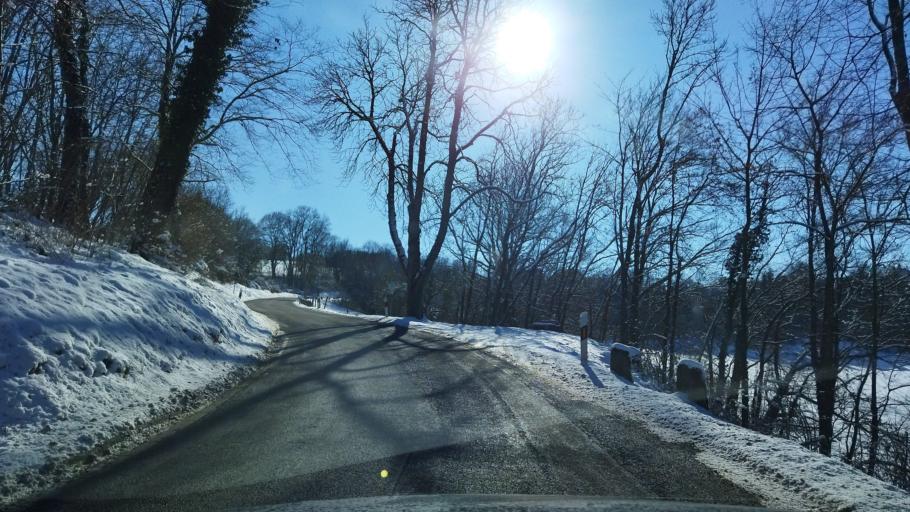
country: DE
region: Baden-Wuerttemberg
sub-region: Regierungsbezirk Stuttgart
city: Ilshofen
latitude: 49.2100
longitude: 9.9235
